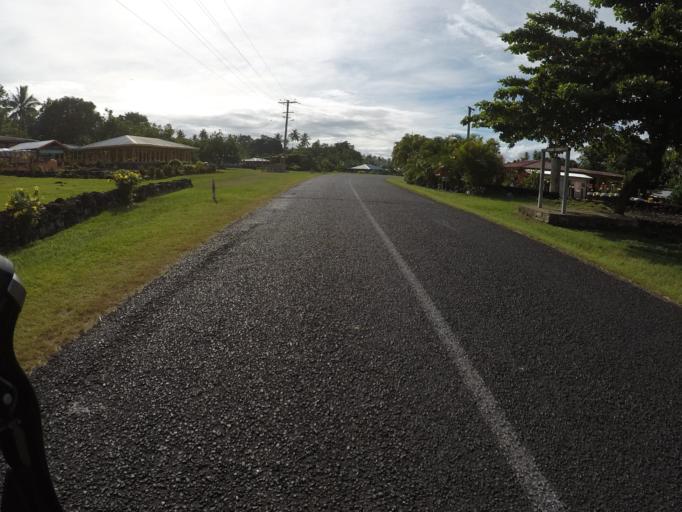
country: WS
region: Vaisigano
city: Asau
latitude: -13.6850
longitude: -172.6203
